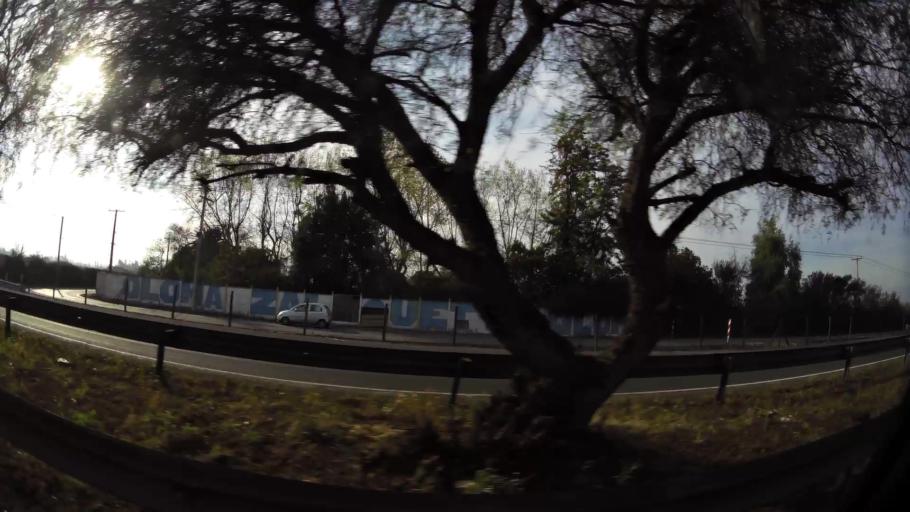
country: CL
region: Santiago Metropolitan
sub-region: Provincia de Talagante
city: Penaflor
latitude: -33.6458
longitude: -70.8777
